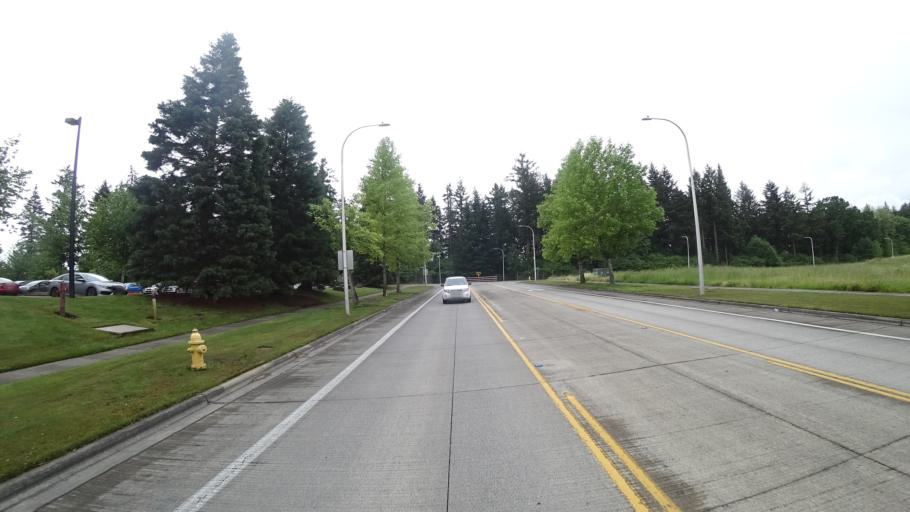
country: US
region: Oregon
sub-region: Washington County
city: Rockcreek
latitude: 45.5276
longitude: -122.8844
